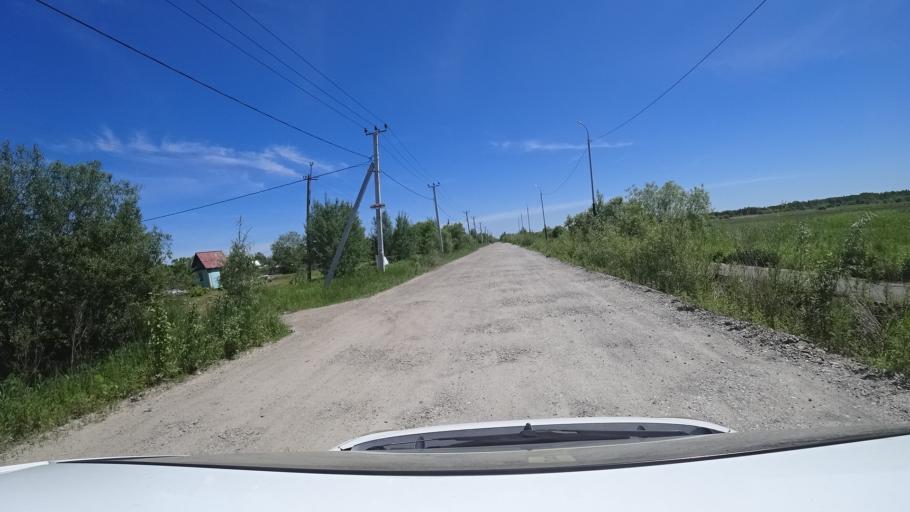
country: RU
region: Khabarovsk Krai
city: Topolevo
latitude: 48.5012
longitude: 135.1902
